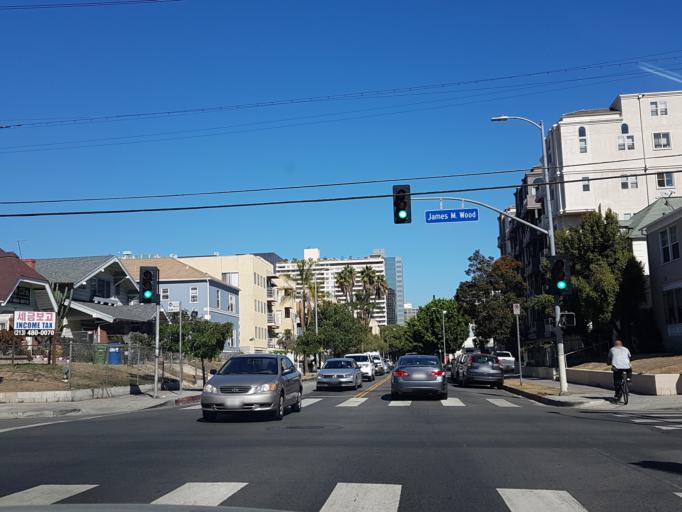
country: US
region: California
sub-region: Los Angeles County
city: Silver Lake
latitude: 34.0558
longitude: -118.3009
